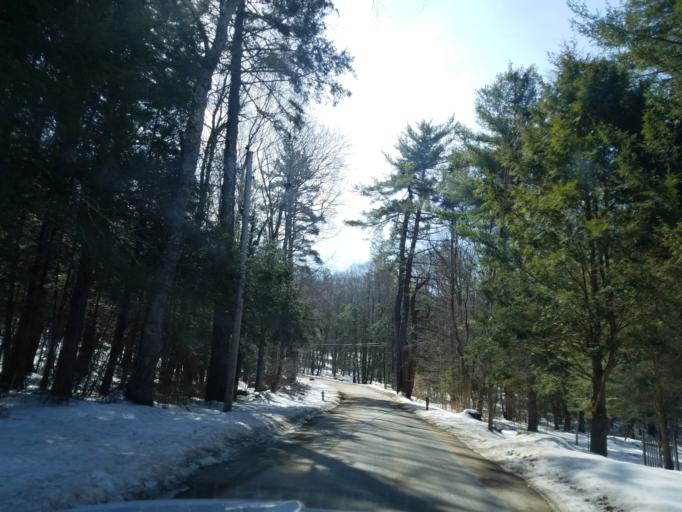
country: US
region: Connecticut
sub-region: Litchfield County
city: Canaan
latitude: 41.8690
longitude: -73.3543
